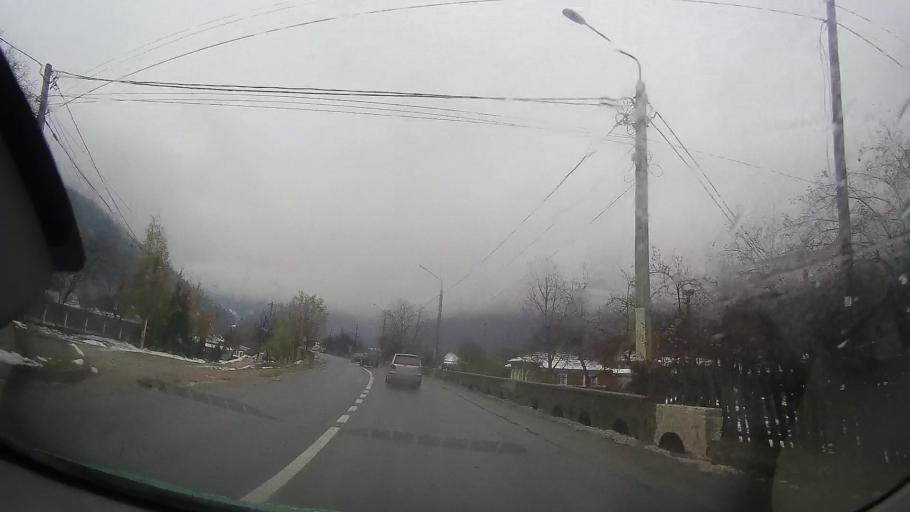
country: RO
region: Neamt
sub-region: Comuna Bicaz
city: Dodeni
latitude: 46.9059
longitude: 26.1080
